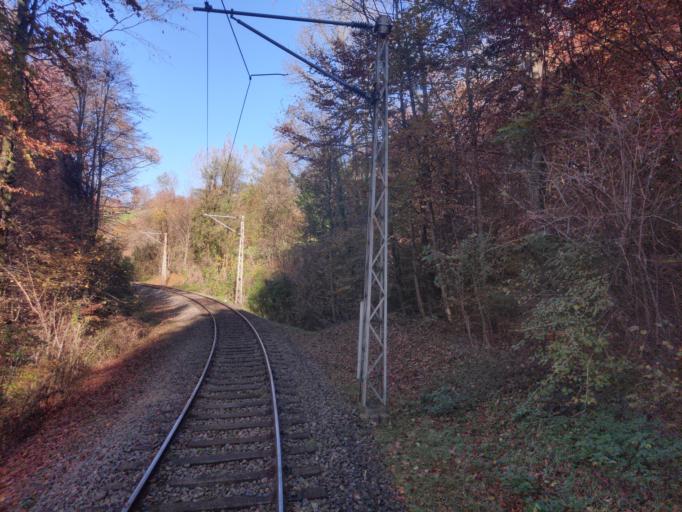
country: AT
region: Styria
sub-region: Politischer Bezirk Suedoststeiermark
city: Maierdorf
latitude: 46.8910
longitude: 15.8641
